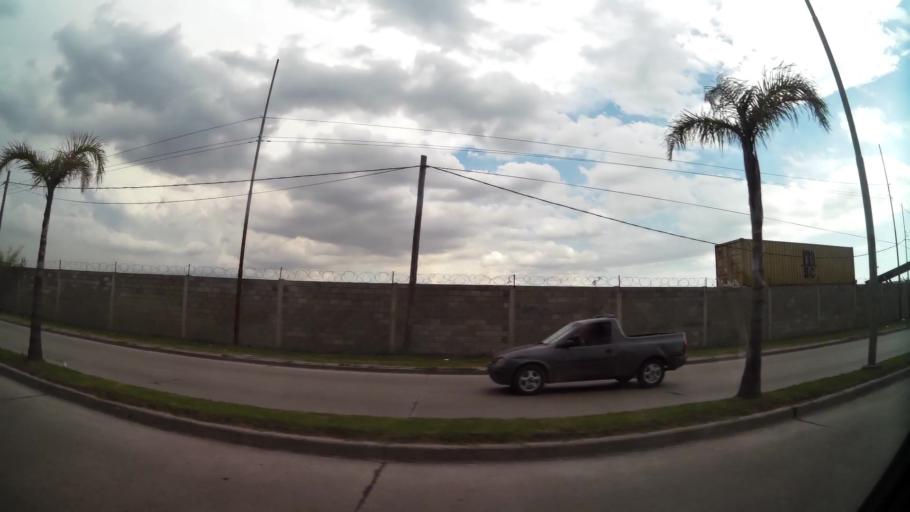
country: AR
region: Buenos Aires
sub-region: Partido de Tigre
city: Tigre
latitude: -34.4807
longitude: -58.6058
